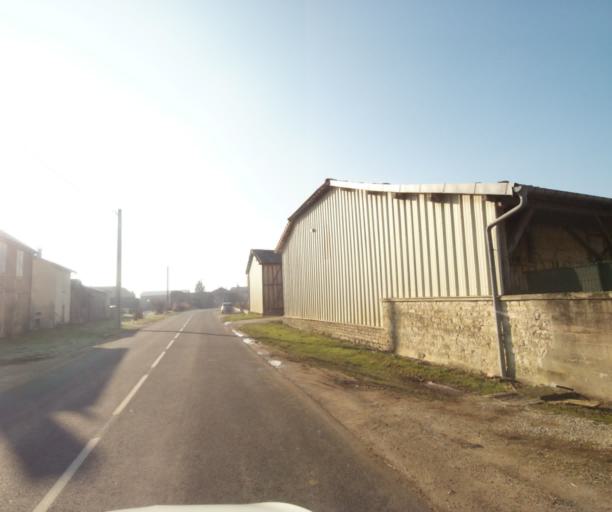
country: FR
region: Champagne-Ardenne
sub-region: Departement de la Haute-Marne
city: Montier-en-Der
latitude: 48.4559
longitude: 4.7690
